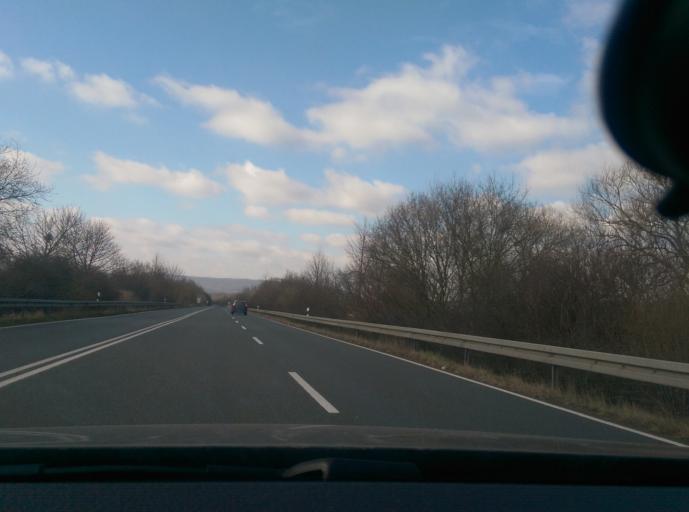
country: DE
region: Lower Saxony
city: Hessisch Oldendorf
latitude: 52.1547
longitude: 9.2774
